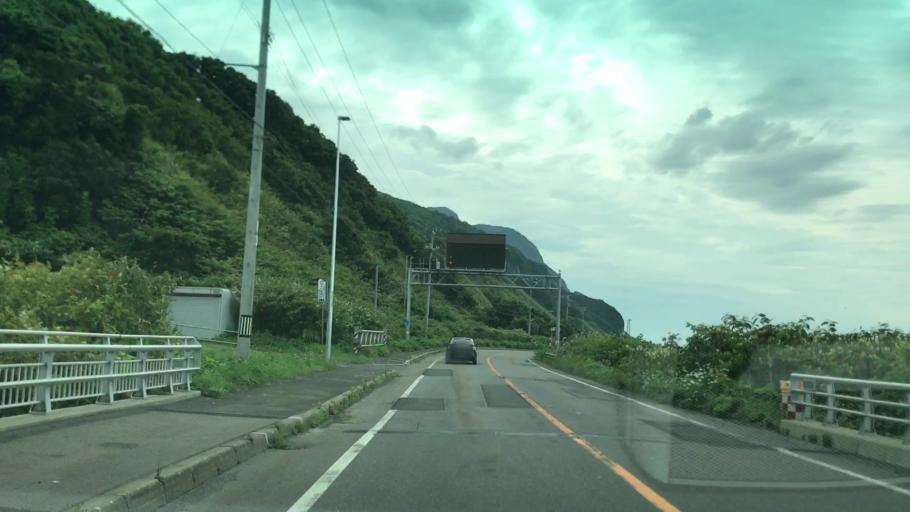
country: JP
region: Hokkaido
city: Iwanai
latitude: 42.9632
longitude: 140.4660
